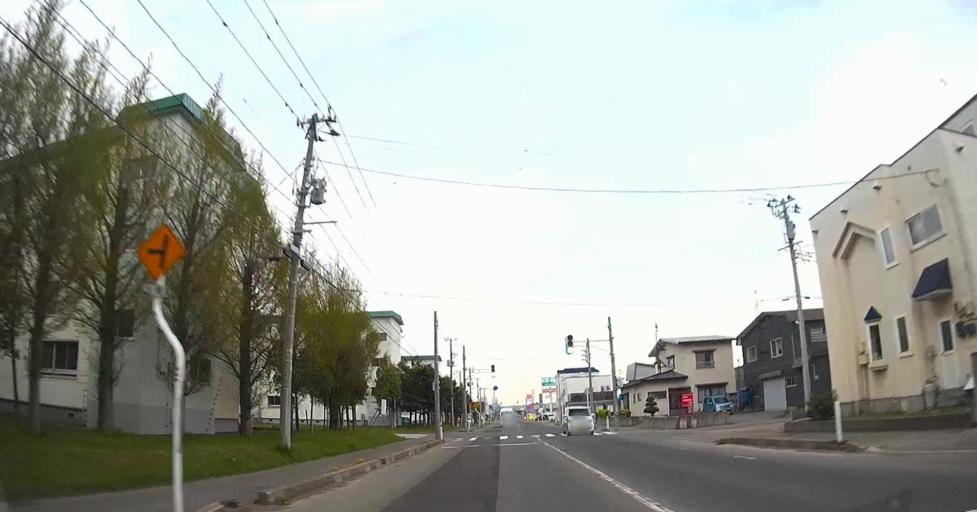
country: JP
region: Aomori
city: Aomori Shi
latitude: 40.8582
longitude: 140.6813
